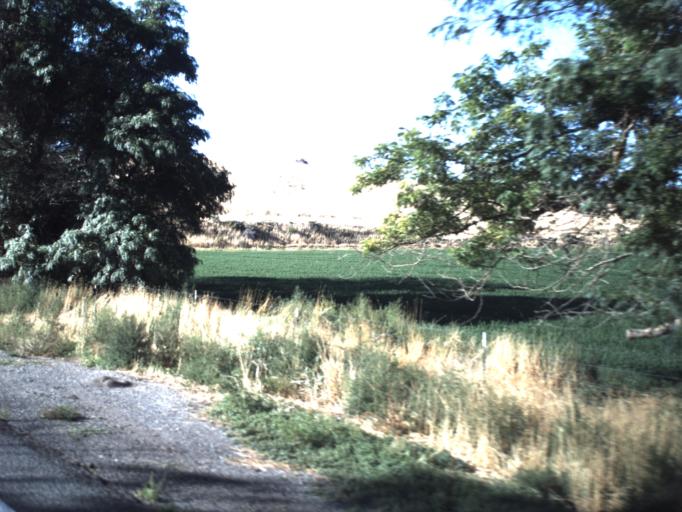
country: US
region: Utah
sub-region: Millard County
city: Delta
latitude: 39.5288
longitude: -112.2734
